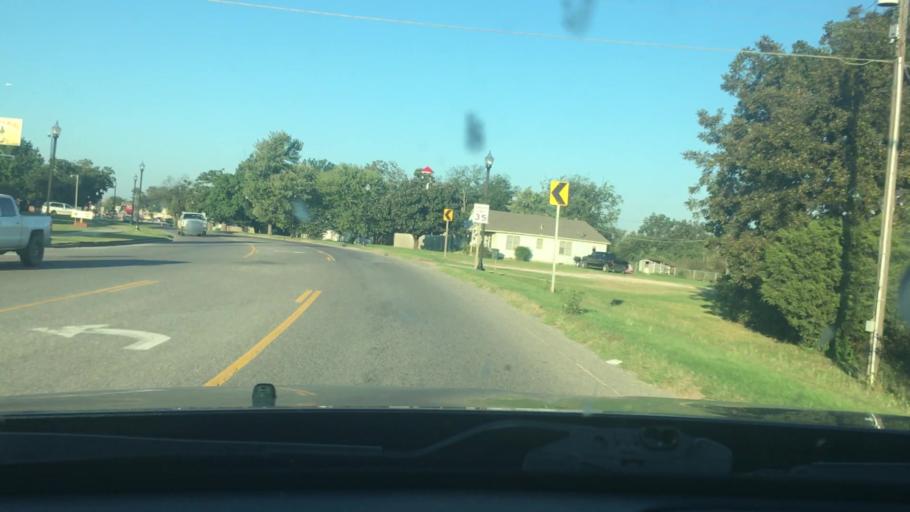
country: US
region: Oklahoma
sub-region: Murray County
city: Davis
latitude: 34.5073
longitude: -97.1108
